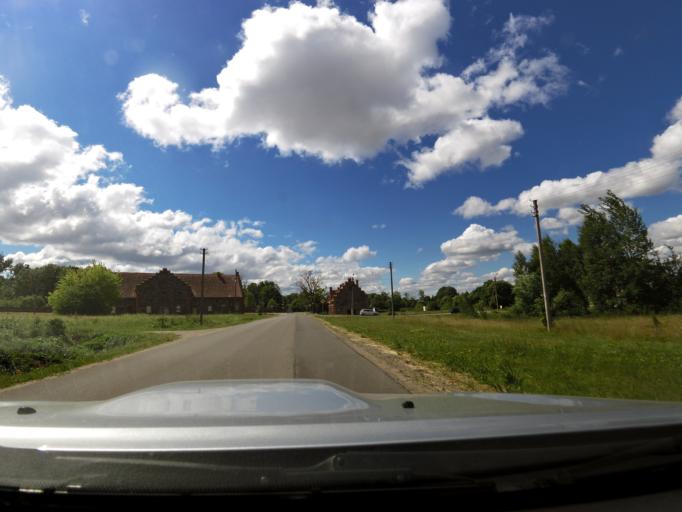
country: LT
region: Panevezys
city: Rokiskis
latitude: 55.9673
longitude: 25.5975
